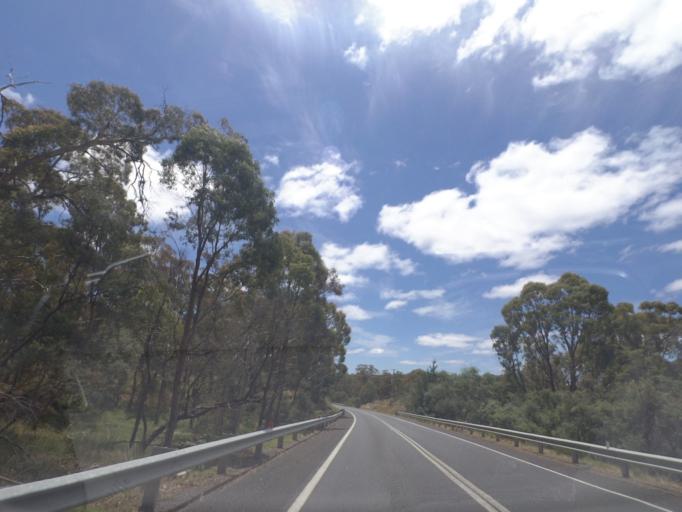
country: AU
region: Victoria
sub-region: Mount Alexander
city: Castlemaine
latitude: -37.2911
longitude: 144.1632
